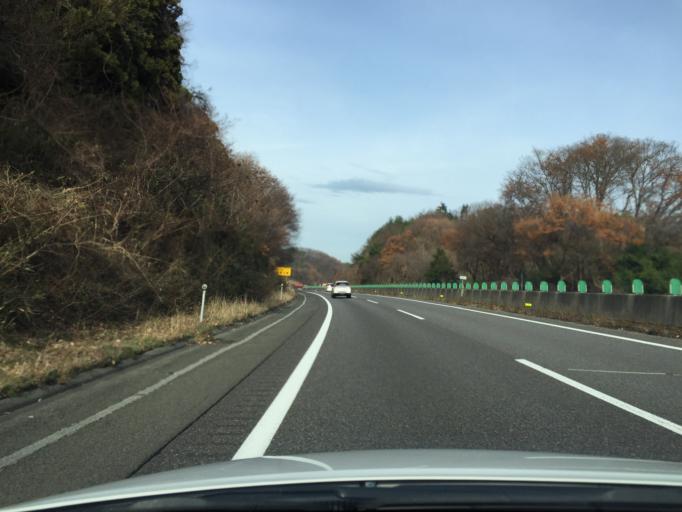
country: JP
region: Fukushima
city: Nihommatsu
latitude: 37.6254
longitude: 140.4314
